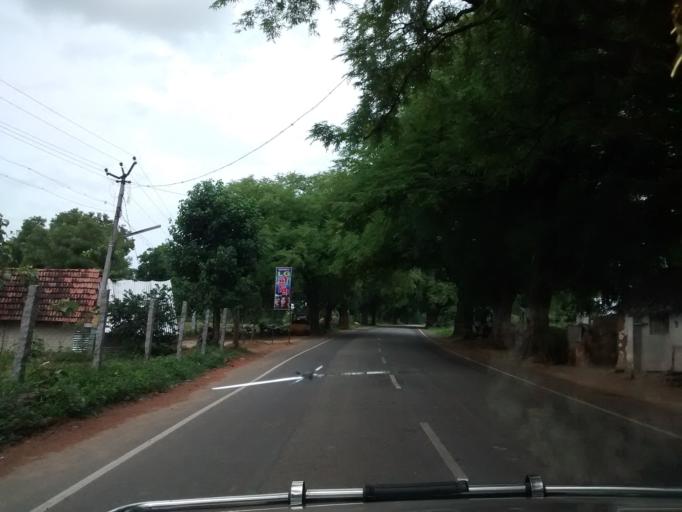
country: IN
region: Andhra Pradesh
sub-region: Chittoor
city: Chittoor
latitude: 13.3178
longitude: 79.0301
